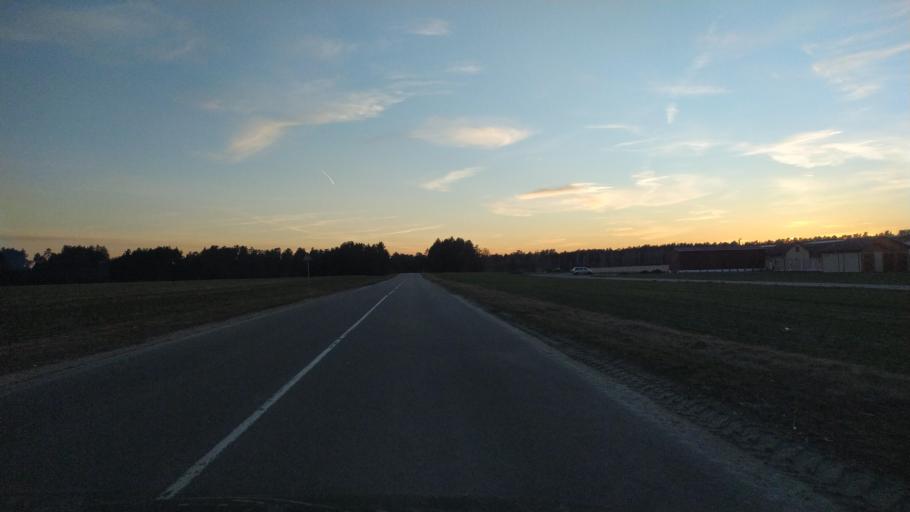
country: BY
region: Brest
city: Pruzhany
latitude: 52.5376
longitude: 24.1990
